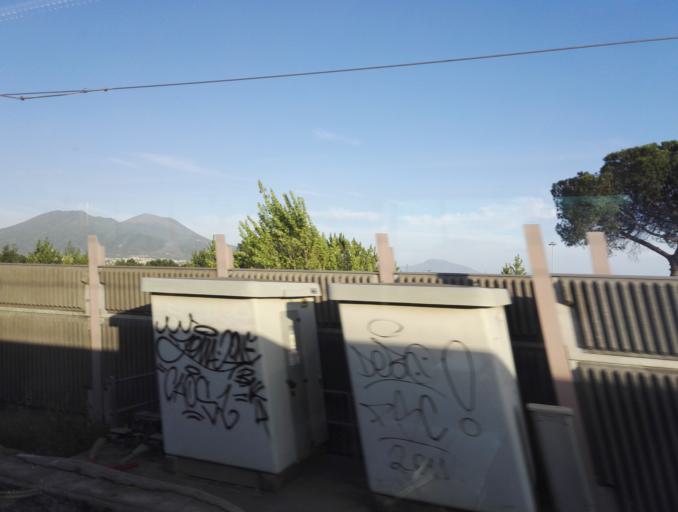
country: IT
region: Campania
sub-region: Provincia di Napoli
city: Arpino
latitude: 40.8708
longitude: 14.3040
